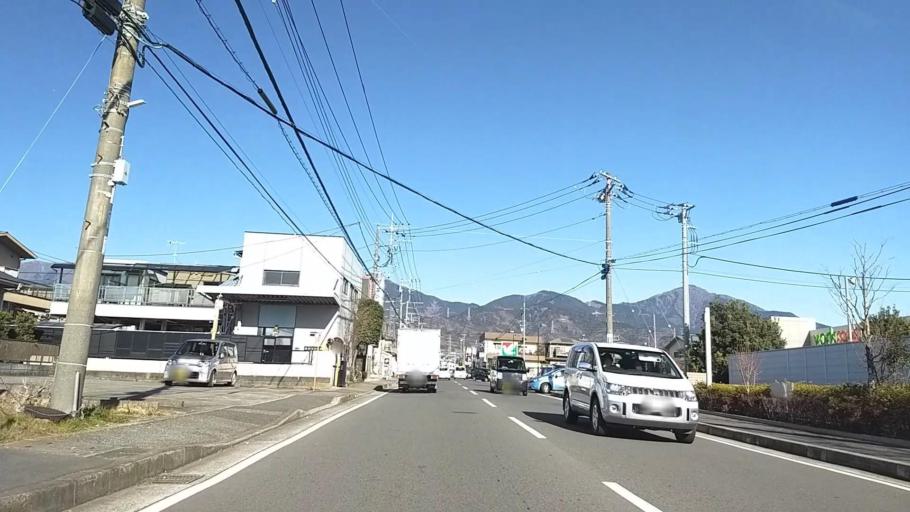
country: JP
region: Kanagawa
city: Hadano
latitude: 35.3739
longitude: 139.2082
